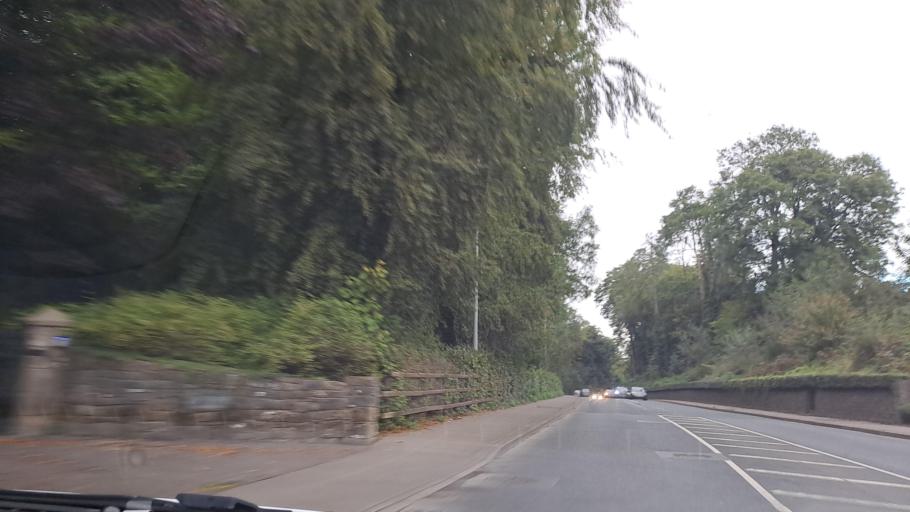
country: IE
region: Ulster
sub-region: County Monaghan
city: Monaghan
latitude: 54.2398
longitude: -6.9688
